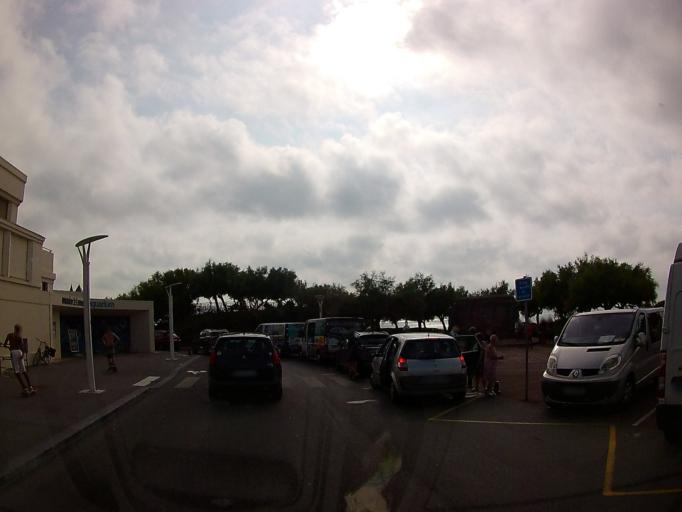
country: FR
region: Aquitaine
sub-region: Departement des Pyrenees-Atlantiques
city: Biarritz
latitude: 43.4842
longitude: -1.5684
